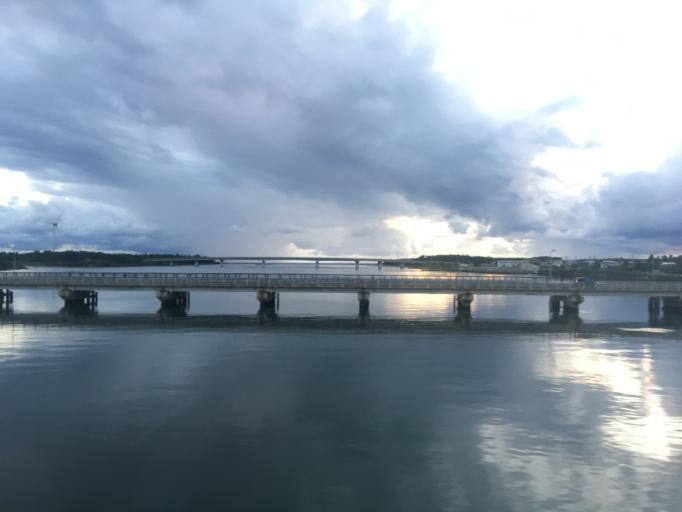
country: JP
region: Akita
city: Tenno
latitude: 39.9020
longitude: 139.9576
